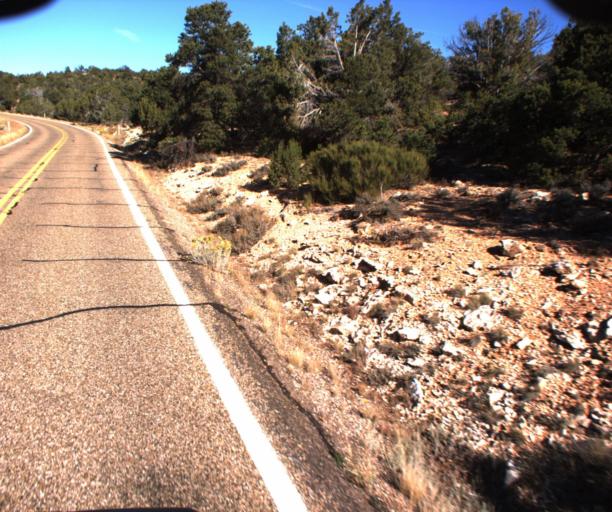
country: US
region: Arizona
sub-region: Coconino County
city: Fredonia
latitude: 36.7405
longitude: -112.1076
